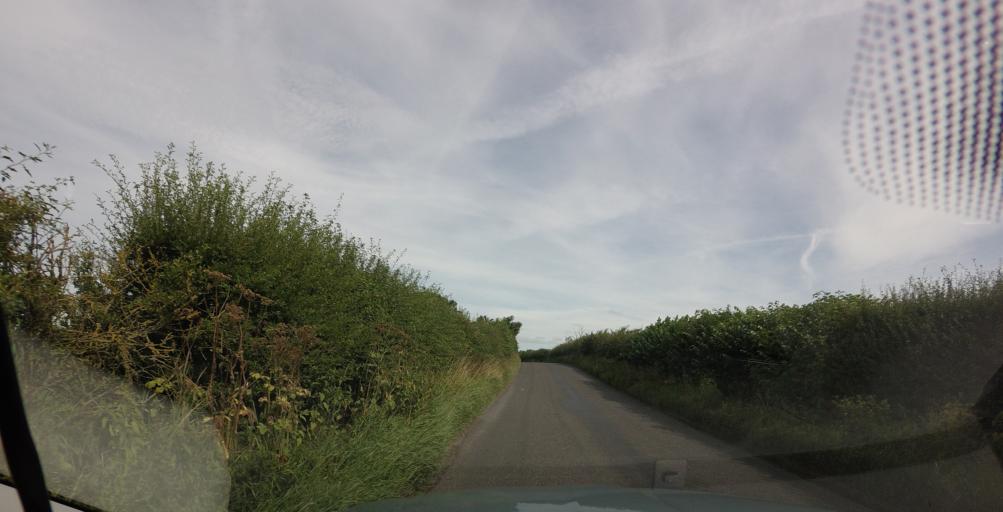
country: GB
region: England
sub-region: North Yorkshire
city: Ripon
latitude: 54.1088
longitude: -1.5164
